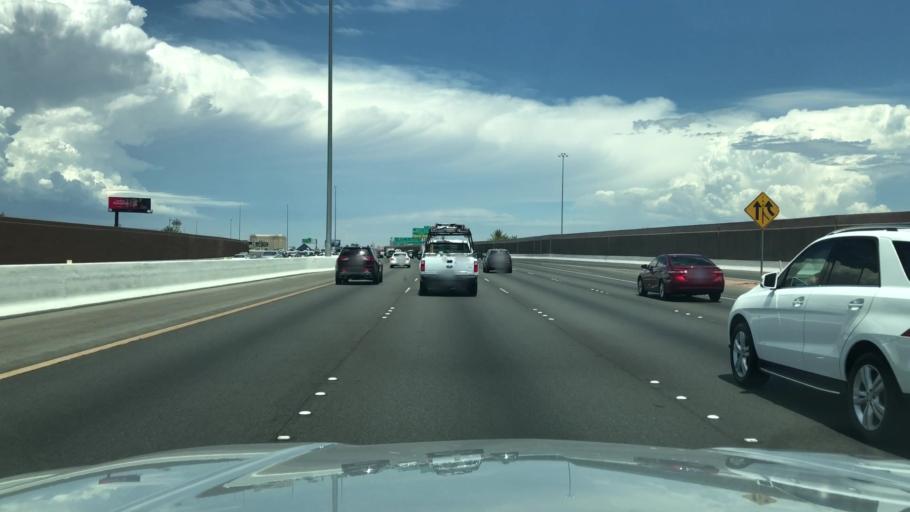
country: US
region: Nevada
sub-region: Clark County
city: Paradise
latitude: 36.0560
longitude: -115.1392
